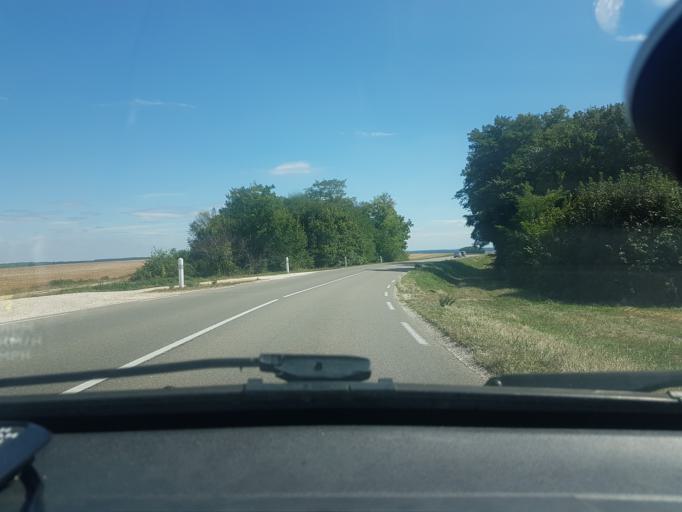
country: FR
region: Bourgogne
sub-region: Departement de la Cote-d'Or
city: Belleneuve
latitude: 47.3844
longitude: 5.2863
